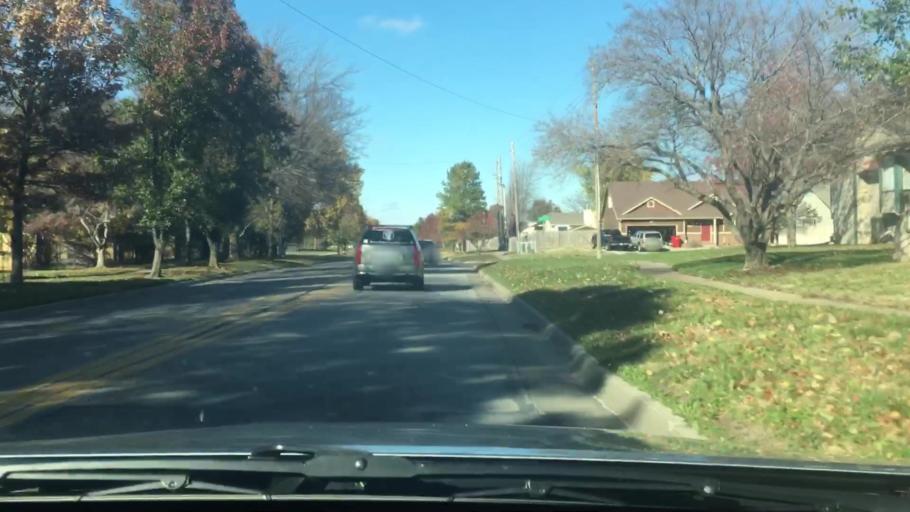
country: US
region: Kansas
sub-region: Sedgwick County
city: Maize
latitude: 37.7142
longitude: -97.4813
